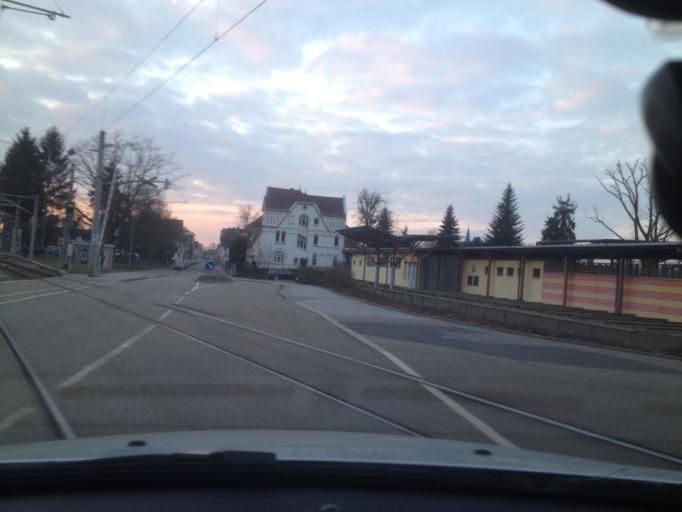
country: DE
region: Baden-Wuerttemberg
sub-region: Karlsruhe Region
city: Ettlingen
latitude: 48.9365
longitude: 8.4172
